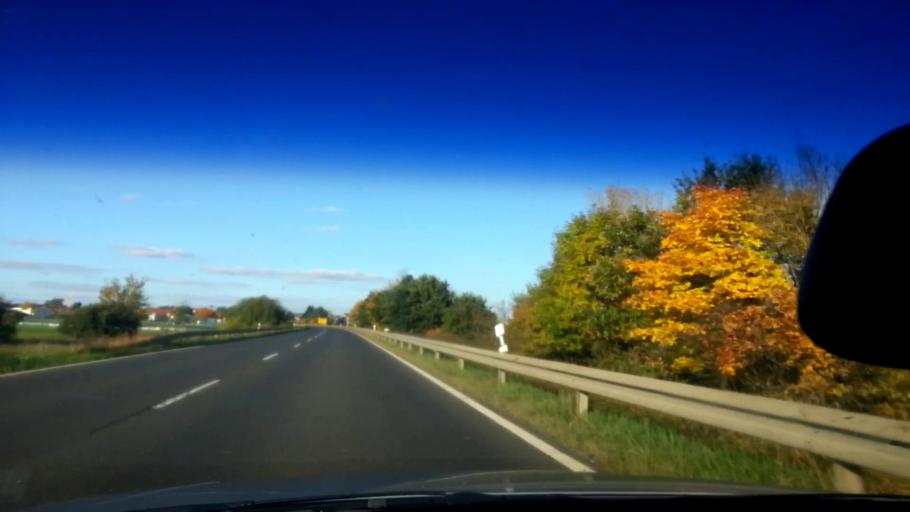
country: DE
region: Bavaria
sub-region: Upper Franconia
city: Rattelsdorf
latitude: 50.0085
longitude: 10.8901
